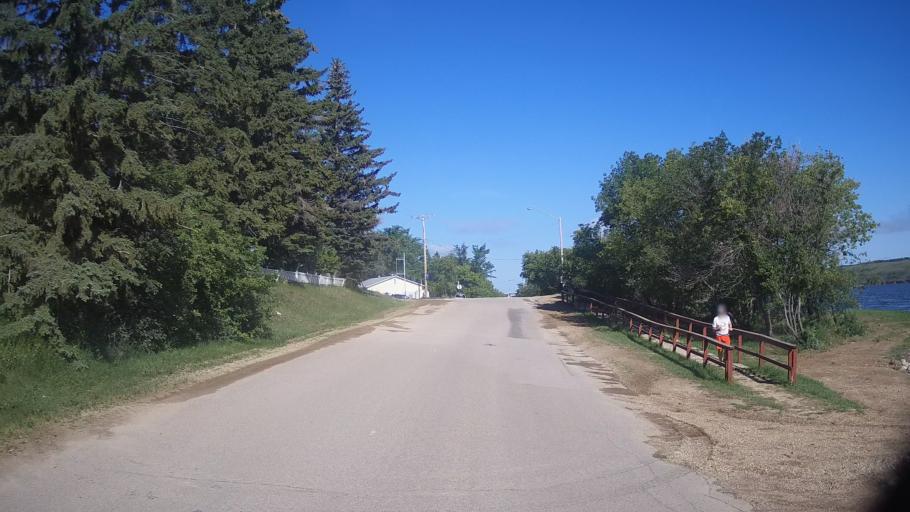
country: CA
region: Saskatchewan
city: Watrous
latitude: 51.7196
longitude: -105.4404
